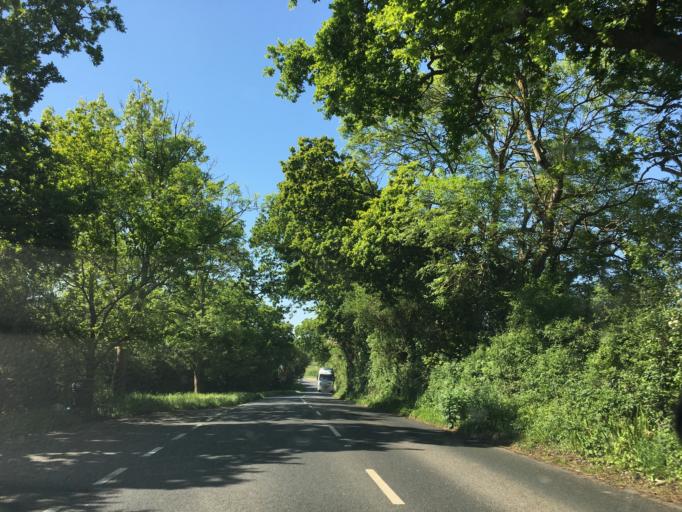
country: GB
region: England
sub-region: Isle of Wight
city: Ryde
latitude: 50.7065
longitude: -1.1658
